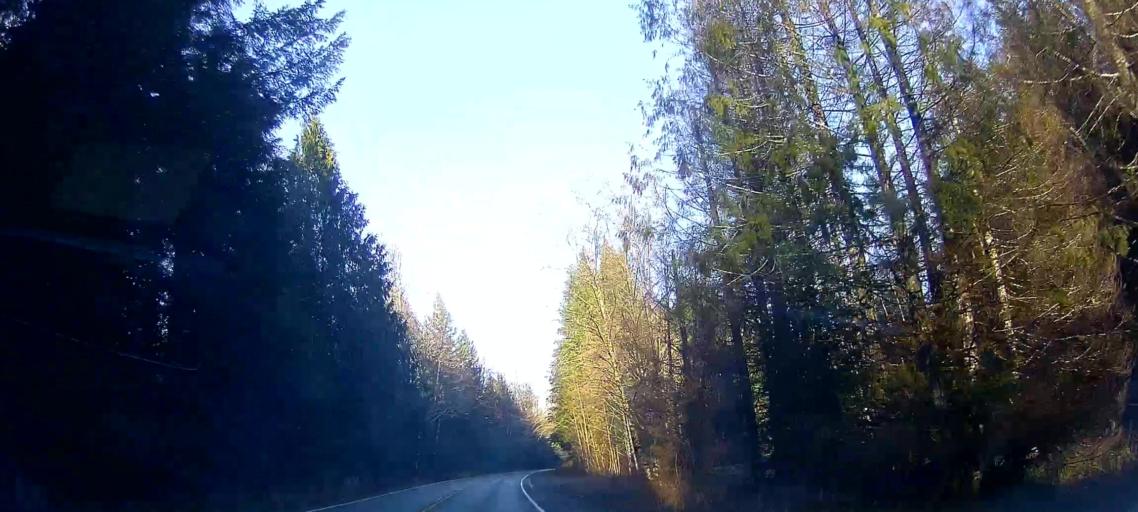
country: US
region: Washington
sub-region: Snohomish County
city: Darrington
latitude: 48.6147
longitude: -121.7532
